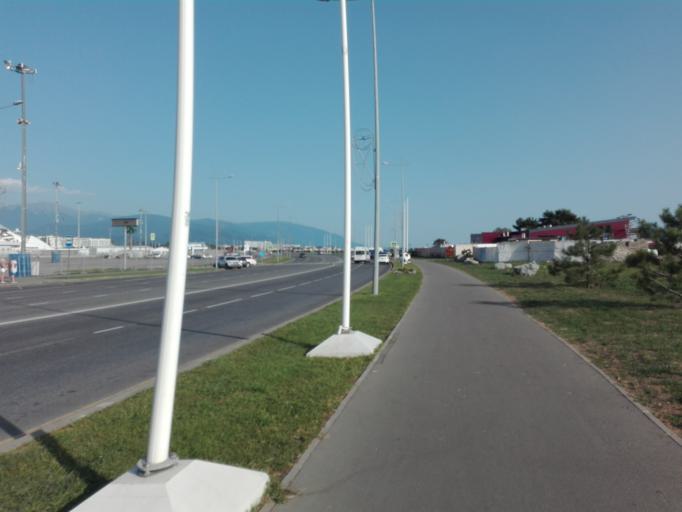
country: RU
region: Krasnodarskiy
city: Adler
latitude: 43.4003
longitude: 39.9496
